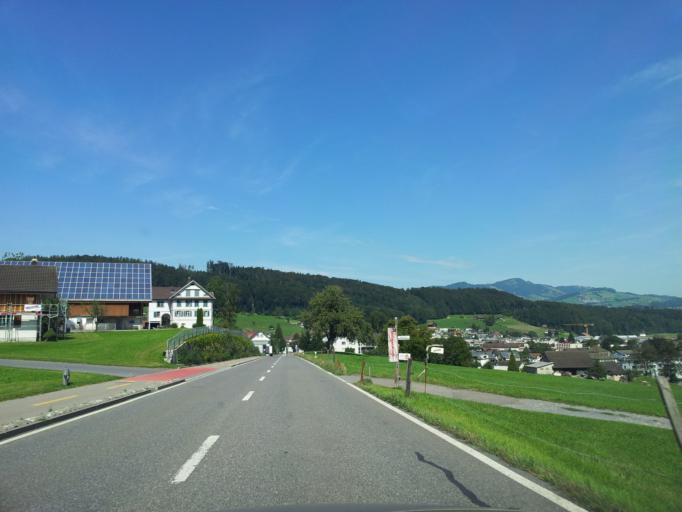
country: CH
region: Schwyz
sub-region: Bezirk March
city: Tuggen
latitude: 47.1959
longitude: 8.9380
